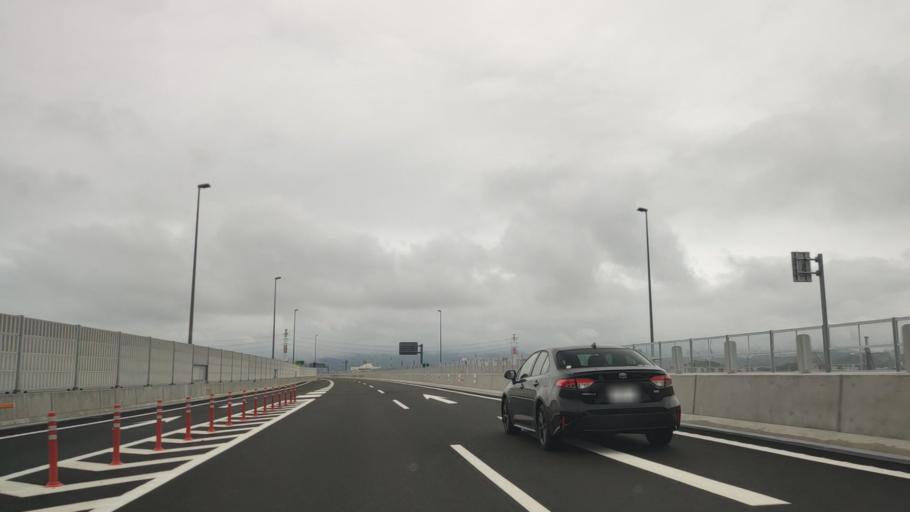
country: JP
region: Kanagawa
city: Atsugi
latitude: 35.4061
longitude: 139.3506
